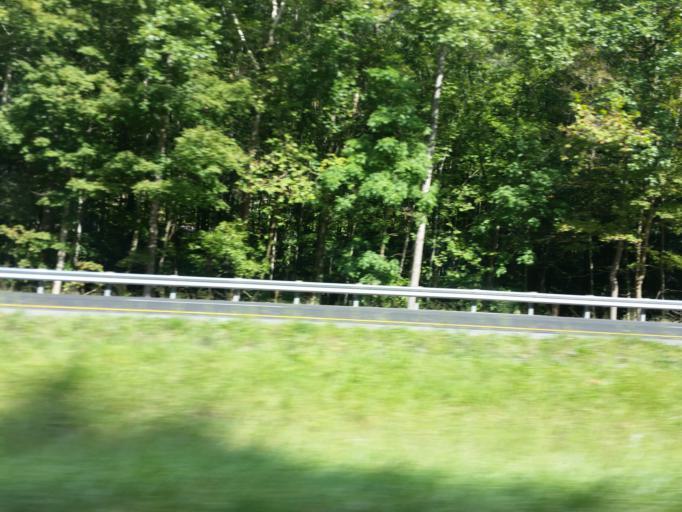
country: US
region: Kentucky
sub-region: Bell County
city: Pineville
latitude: 36.6877
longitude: -83.6847
